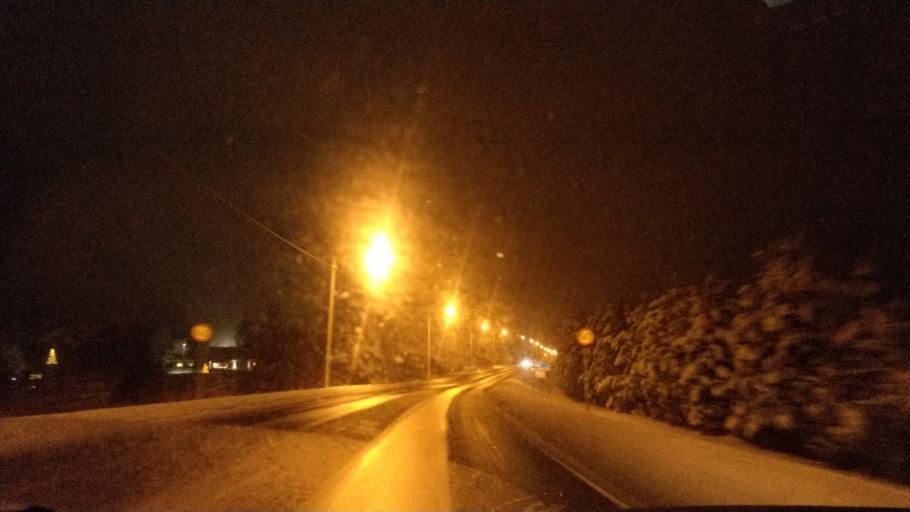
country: FI
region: Lapland
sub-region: Rovaniemi
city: Rovaniemi
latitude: 66.4660
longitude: 25.6081
